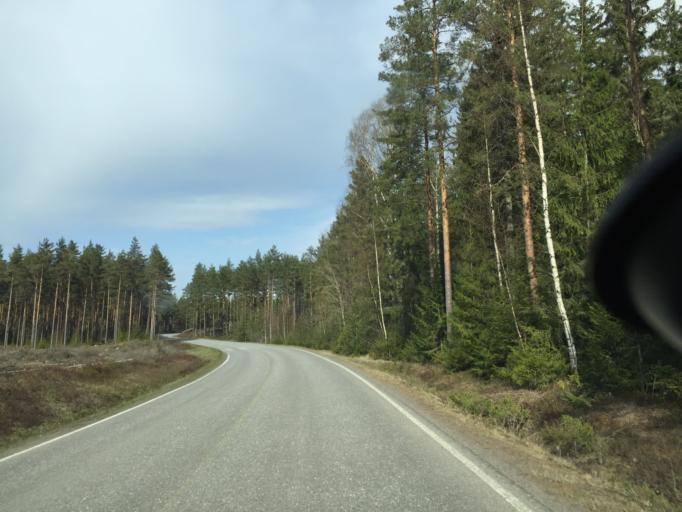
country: FI
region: Uusimaa
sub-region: Raaseporin
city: Hanko
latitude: 59.9626
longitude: 22.9725
